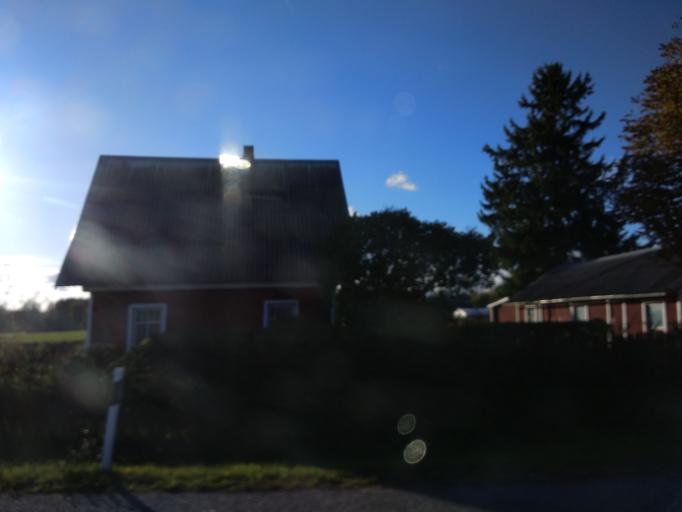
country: EE
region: Polvamaa
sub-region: Polva linn
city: Polva
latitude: 58.0214
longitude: 27.0628
